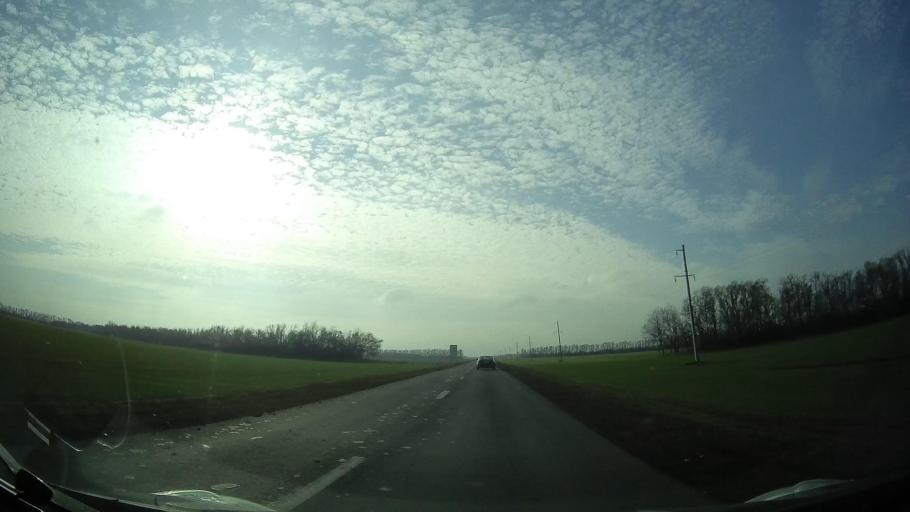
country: RU
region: Rostov
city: Mechetinskaya
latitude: 46.8138
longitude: 40.5435
